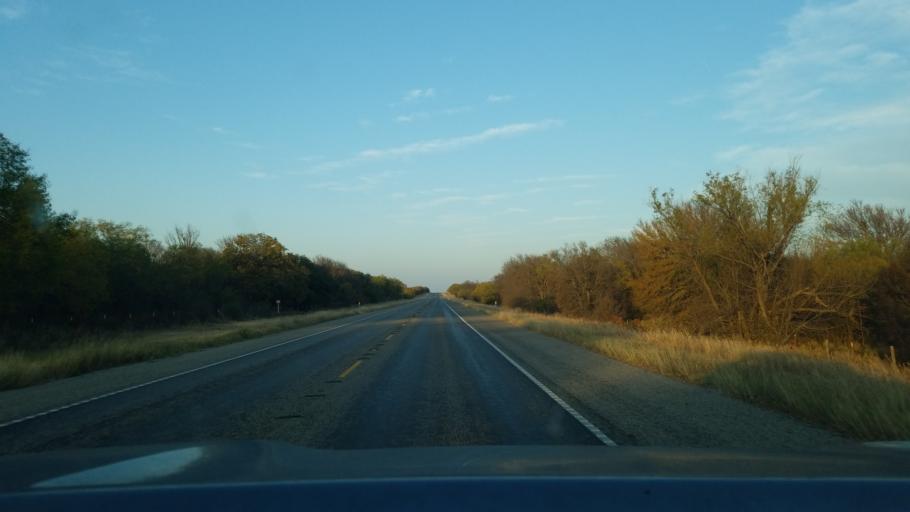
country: US
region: Texas
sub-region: Eastland County
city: Cisco
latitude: 32.4231
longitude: -98.9344
